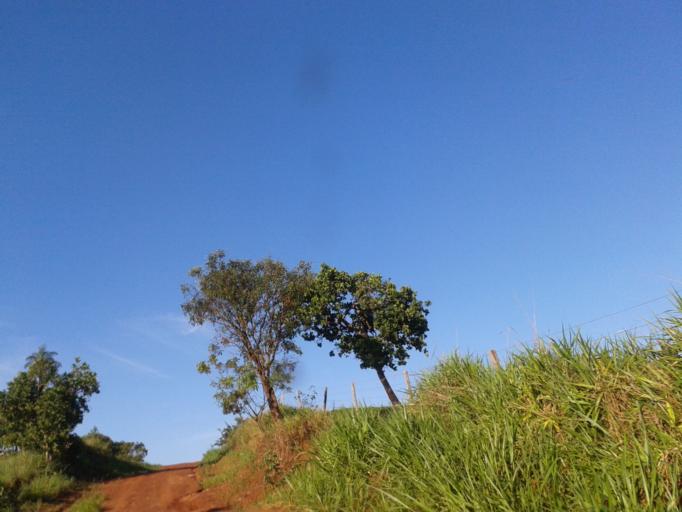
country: BR
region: Minas Gerais
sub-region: Santa Vitoria
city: Santa Vitoria
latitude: -18.9657
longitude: -49.8759
